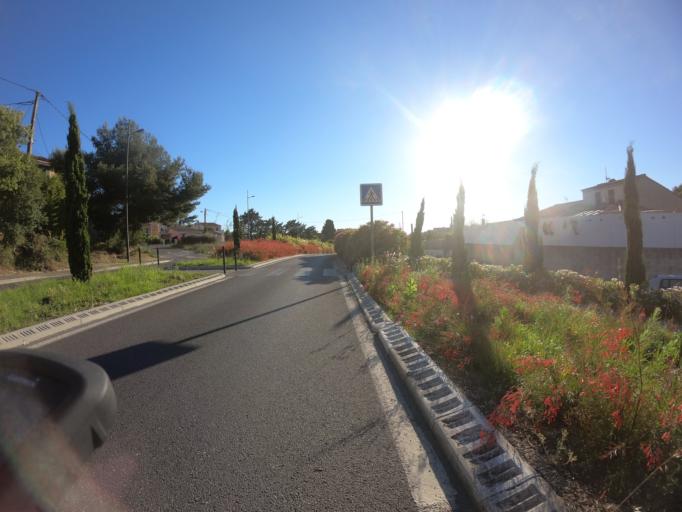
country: FR
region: Provence-Alpes-Cote d'Azur
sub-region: Departement du Var
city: Six-Fours-les-Plages
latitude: 43.1079
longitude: 5.8340
